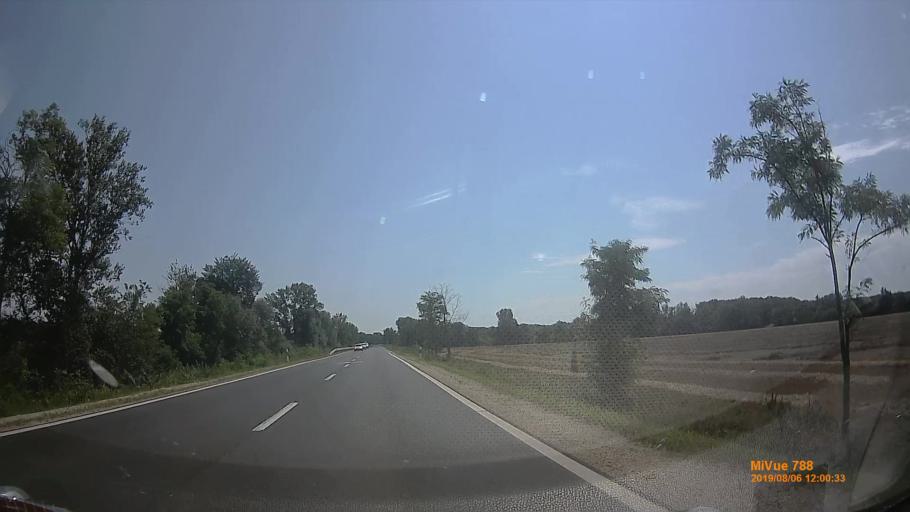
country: HU
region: Vas
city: Vasvar
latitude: 47.0616
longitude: 16.7492
